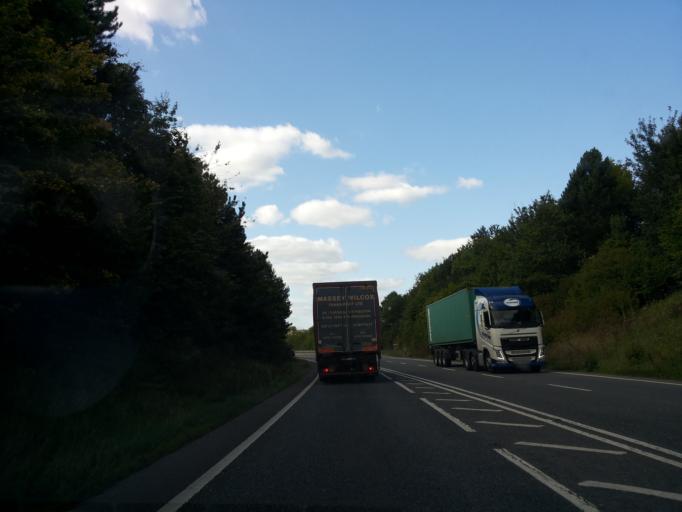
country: GB
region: England
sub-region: Wiltshire
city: Boreham
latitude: 51.1903
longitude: -2.1716
